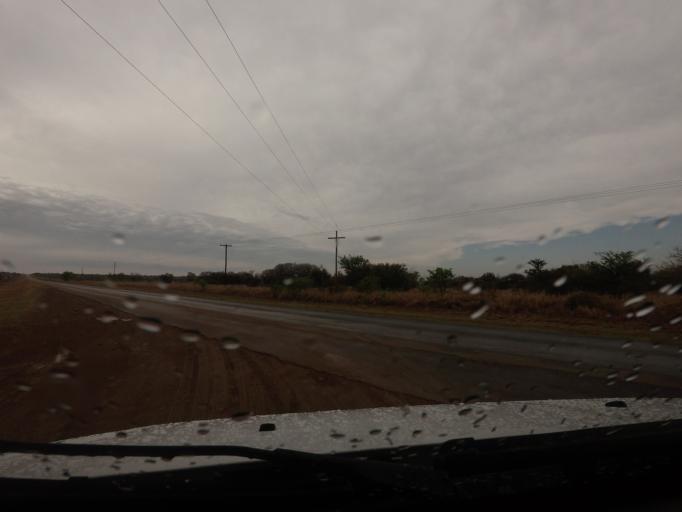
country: ZA
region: Gauteng
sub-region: City of Tshwane Metropolitan Municipality
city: Cullinan
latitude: -25.5668
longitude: 28.3919
